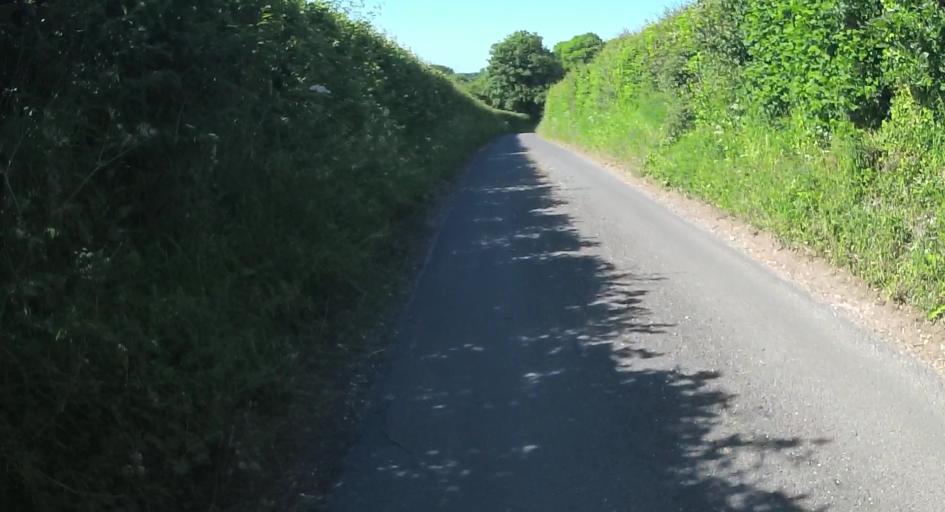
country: GB
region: England
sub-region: Hampshire
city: Overton
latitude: 51.2459
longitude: -1.3100
